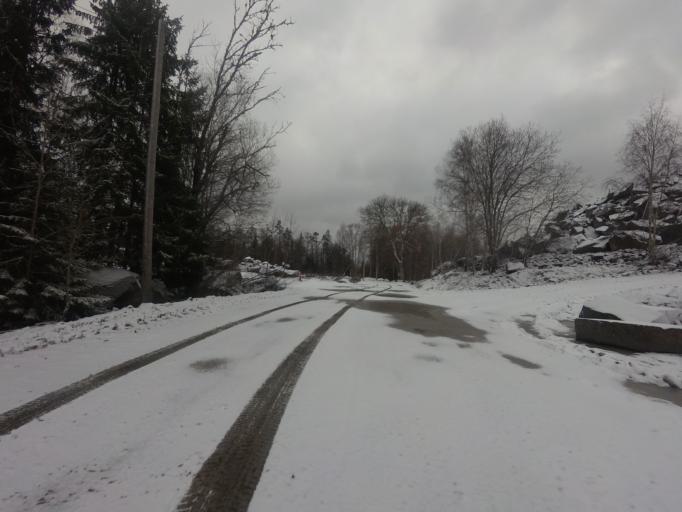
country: SE
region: Skane
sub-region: Osby Kommun
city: Lonsboda
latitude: 56.3985
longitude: 14.2519
